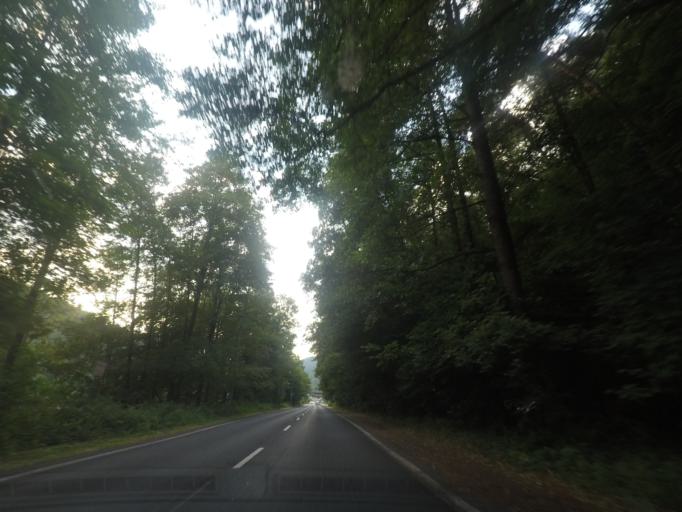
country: DE
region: Saxony
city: Bad Schandau
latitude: 50.8869
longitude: 14.2352
